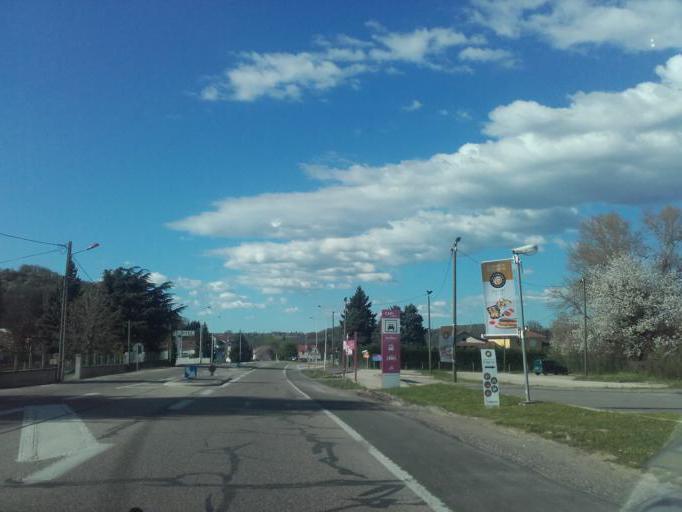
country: FR
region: Rhone-Alpes
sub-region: Departement de l'Isere
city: Nivolas-Vermelle
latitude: 45.5719
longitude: 5.3018
